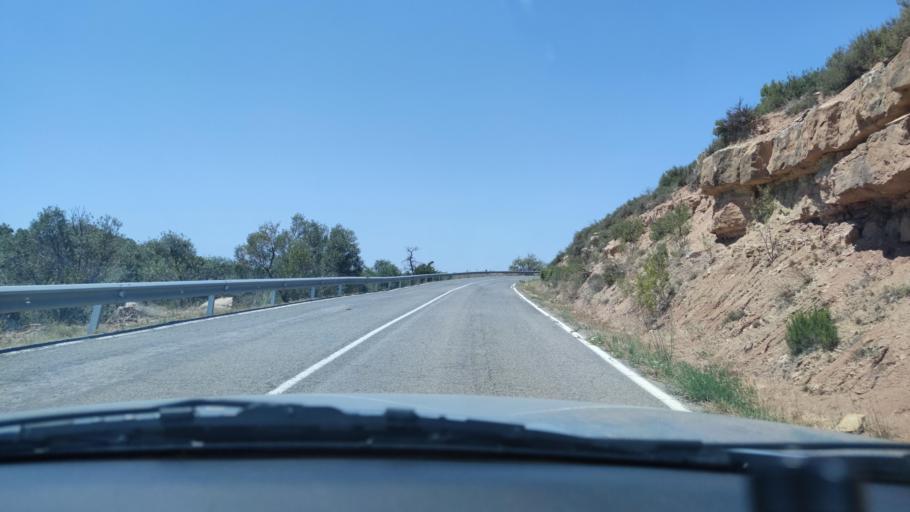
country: ES
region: Catalonia
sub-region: Provincia de Lleida
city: el Cogul
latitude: 41.4266
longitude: 0.6664
